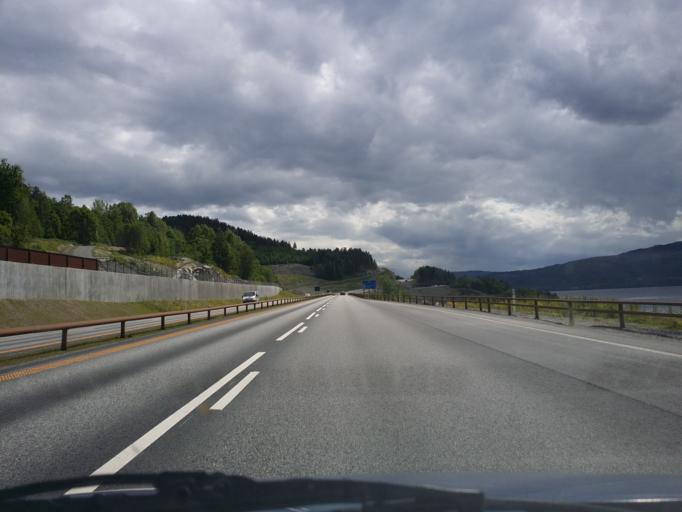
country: NO
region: Akershus
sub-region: Eidsvoll
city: Eidsvoll
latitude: 60.5116
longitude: 11.2434
